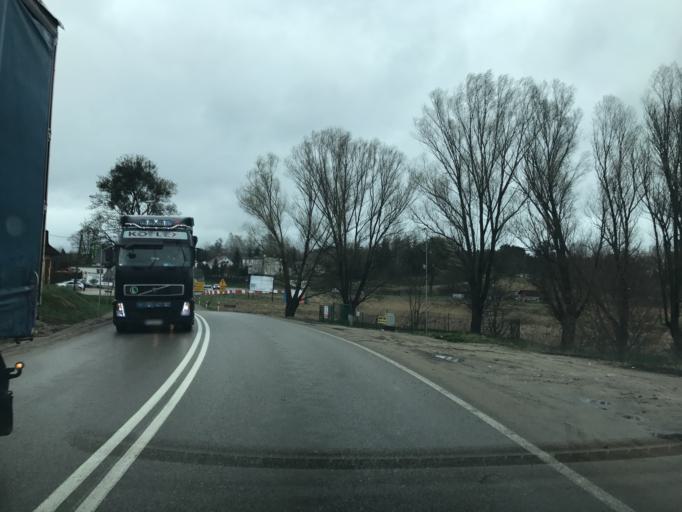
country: PL
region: Warmian-Masurian Voivodeship
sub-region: Powiat ostrodzki
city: Ostroda
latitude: 53.7049
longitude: 19.9787
